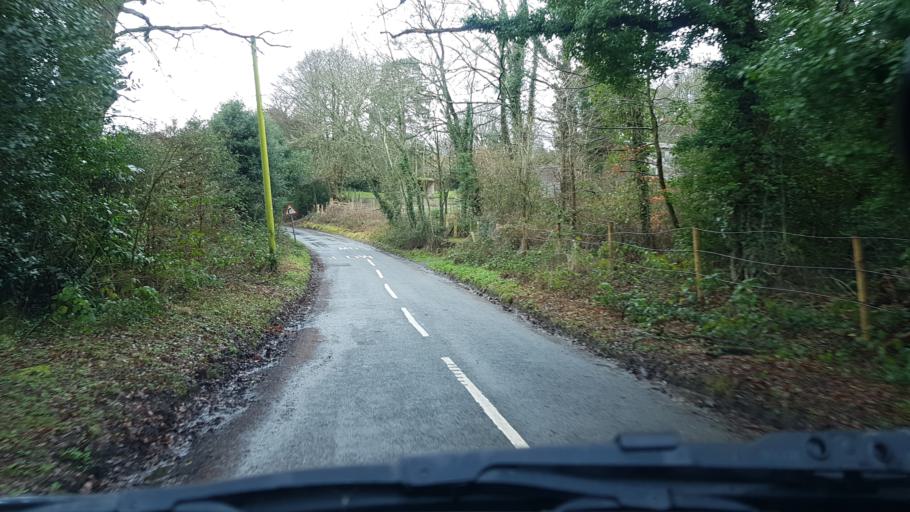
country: GB
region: England
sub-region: Surrey
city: Haslemere
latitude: 51.0957
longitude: -0.6900
